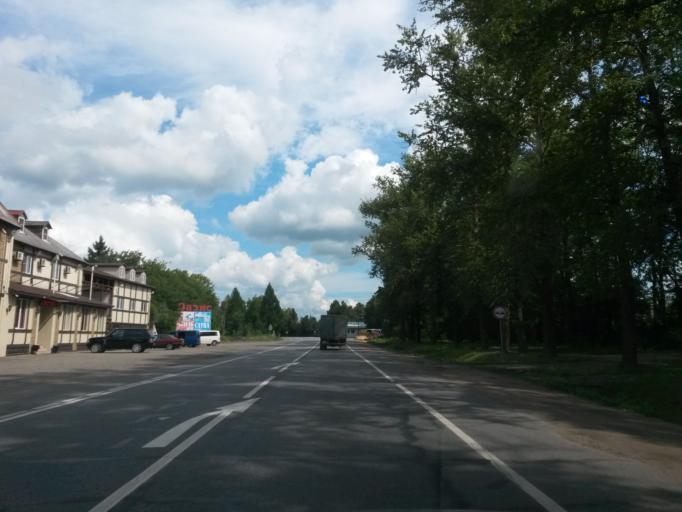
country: RU
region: Jaroslavl
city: Pereslavl'-Zalesskiy
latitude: 56.6507
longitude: 38.6968
